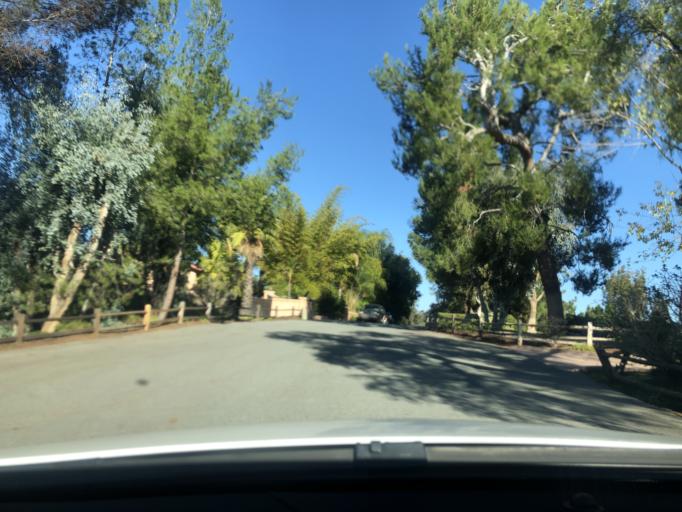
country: US
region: California
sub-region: San Diego County
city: Rancho San Diego
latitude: 32.7677
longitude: -116.9396
